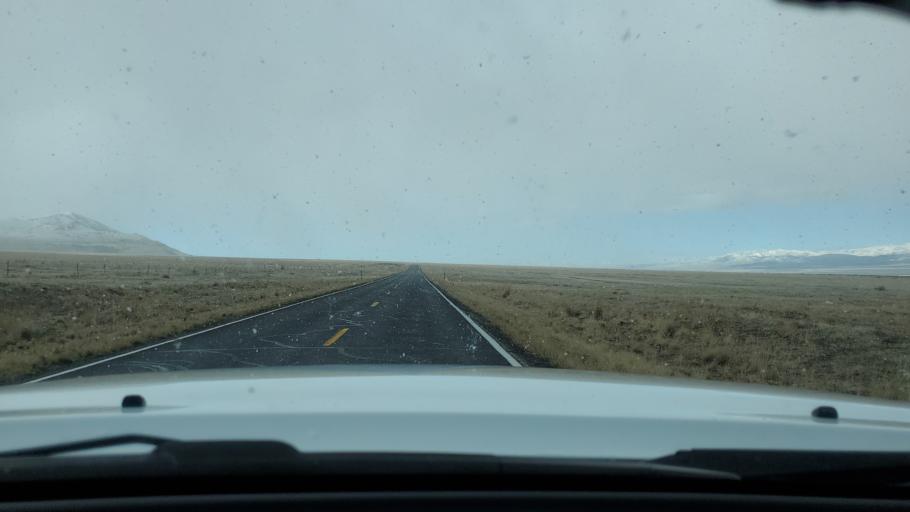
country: US
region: Utah
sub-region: Tooele County
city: Grantsville
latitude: 40.6063
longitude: -112.7082
